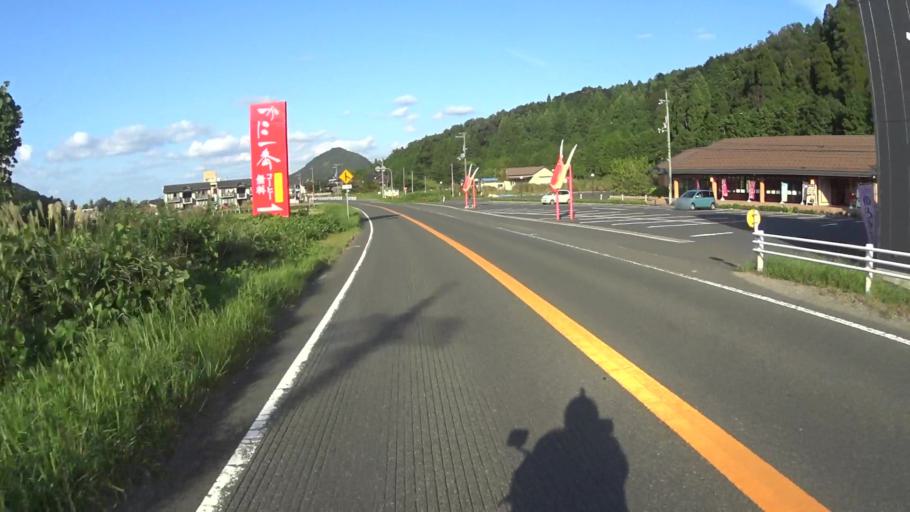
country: JP
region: Hyogo
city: Toyooka
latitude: 35.5861
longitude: 134.8666
